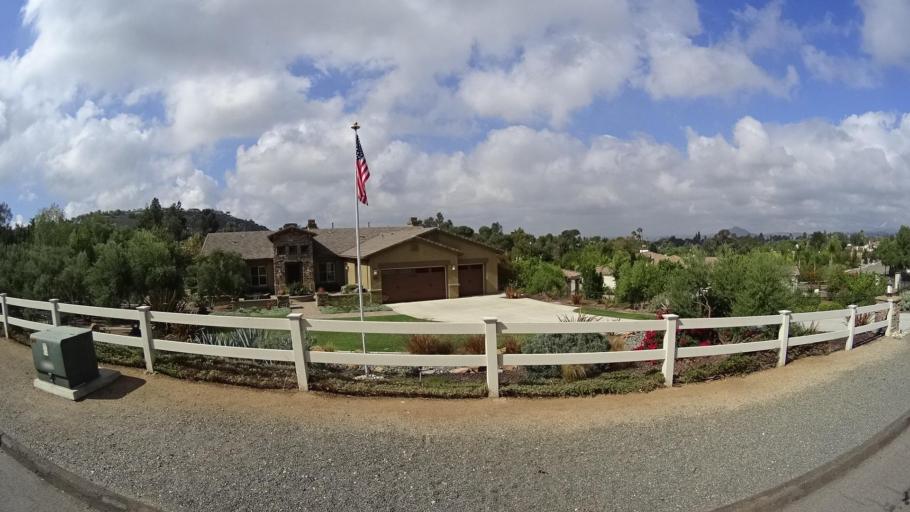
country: US
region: California
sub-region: San Diego County
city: Granite Hills
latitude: 32.7809
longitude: -116.9026
